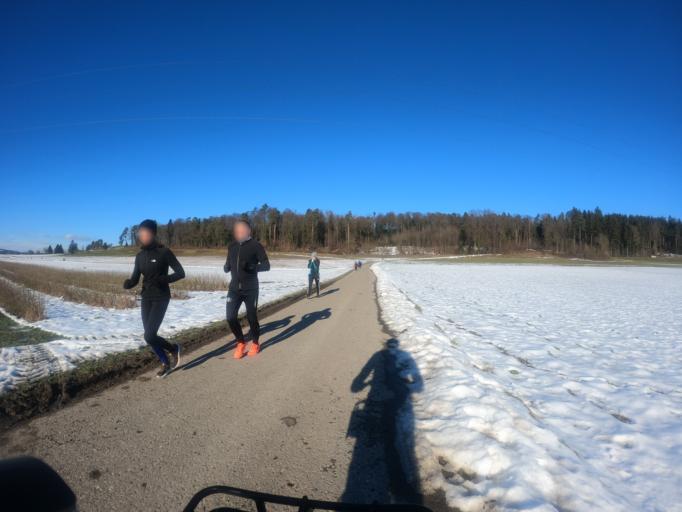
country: CH
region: Aargau
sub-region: Bezirk Bremgarten
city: Berikon
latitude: 47.3345
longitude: 8.3616
